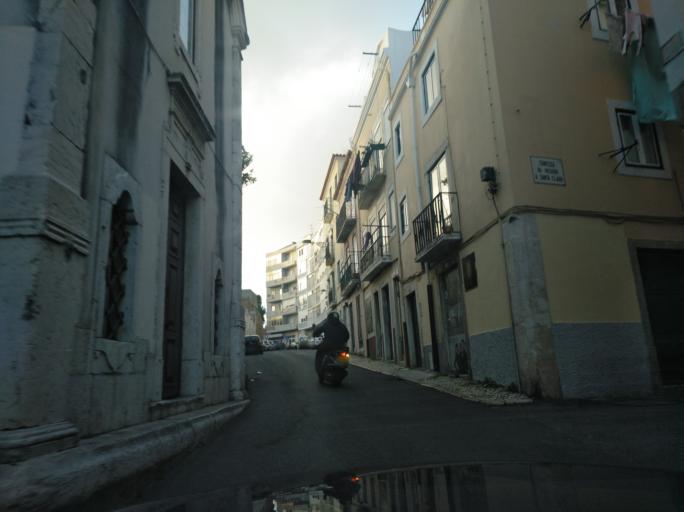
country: PT
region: Lisbon
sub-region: Lisbon
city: Lisbon
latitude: 38.7165
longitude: -9.1259
